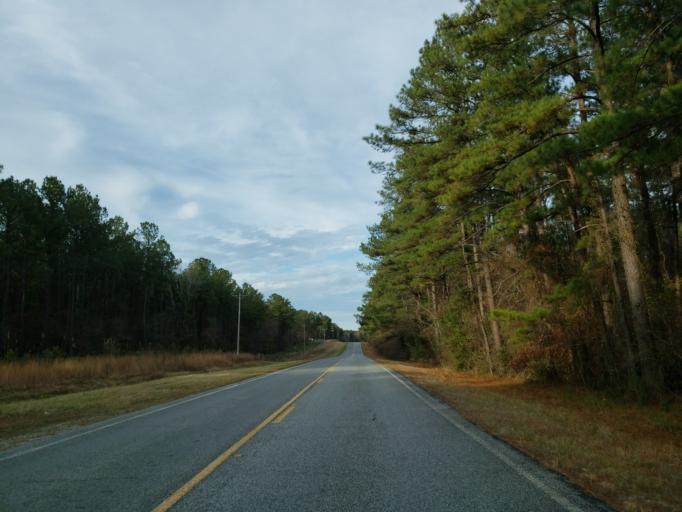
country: US
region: Mississippi
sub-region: Wayne County
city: Waynesboro
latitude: 31.8312
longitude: -88.6897
